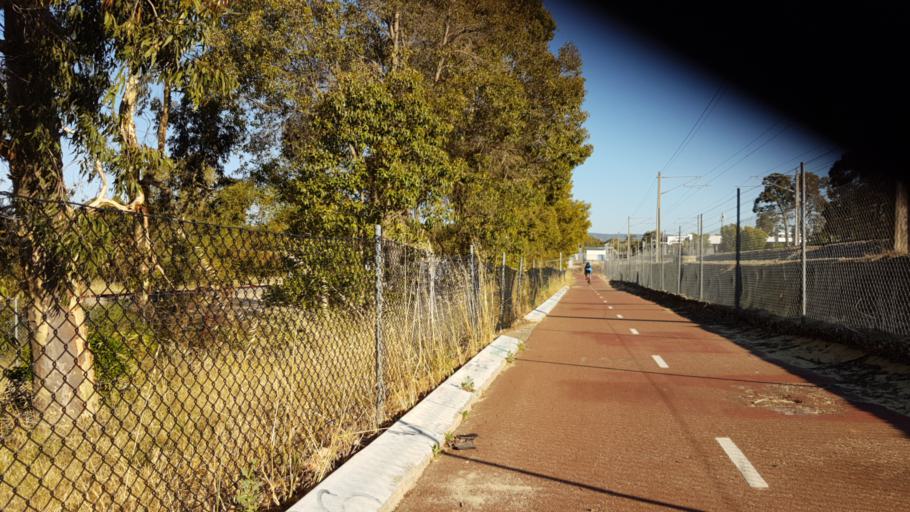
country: AU
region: Western Australia
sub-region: Gosnells
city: Kenwick
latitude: -32.0342
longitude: 115.9673
